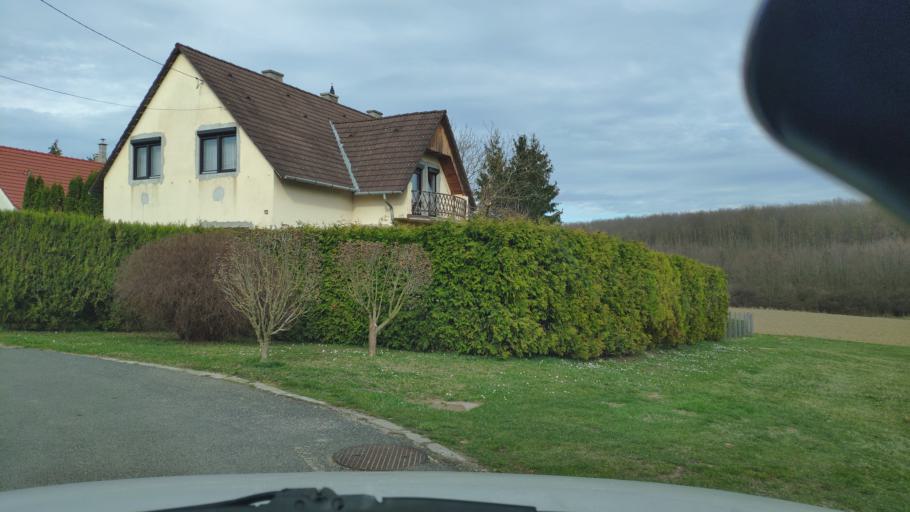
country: HU
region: Zala
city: Nagykanizsa
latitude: 46.4817
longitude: 16.9904
